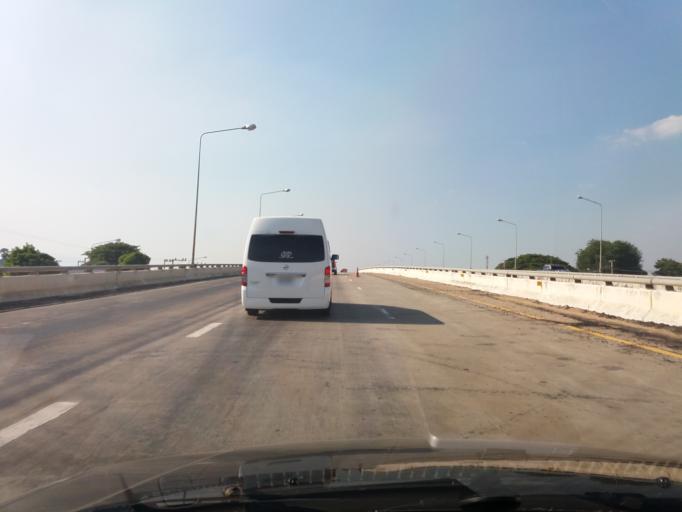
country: TH
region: Nakhon Sawan
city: Nakhon Sawan
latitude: 15.6319
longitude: 100.1027
